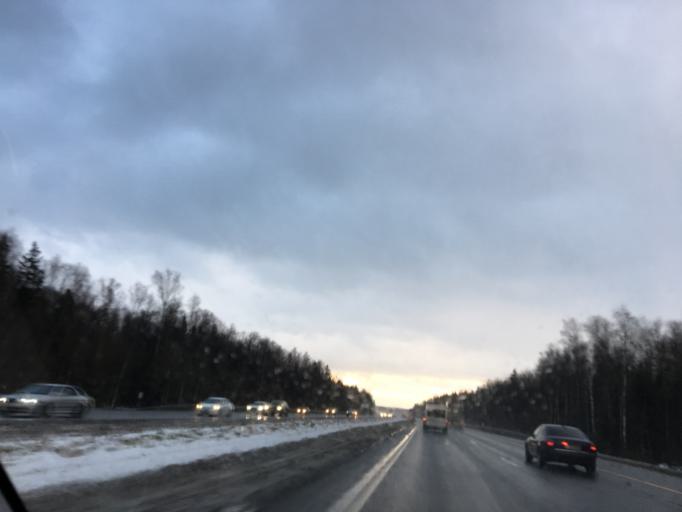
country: RU
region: Moskovskaya
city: Danki
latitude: 54.9666
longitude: 37.5292
